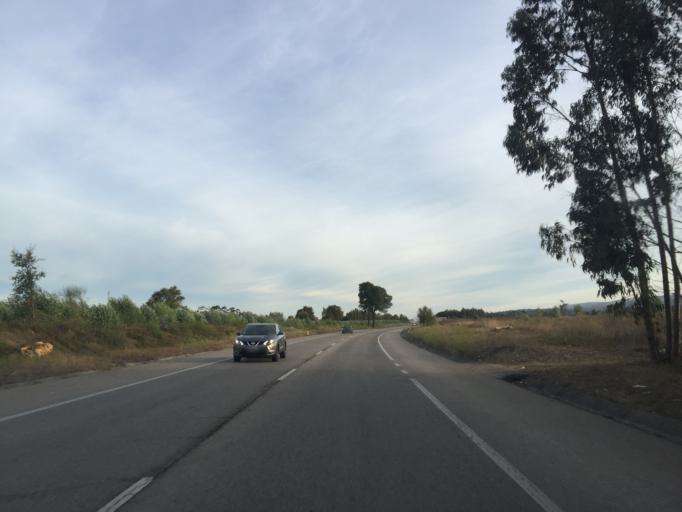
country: PT
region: Leiria
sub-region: Alcobaca
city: Benedita
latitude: 39.4183
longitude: -8.9632
